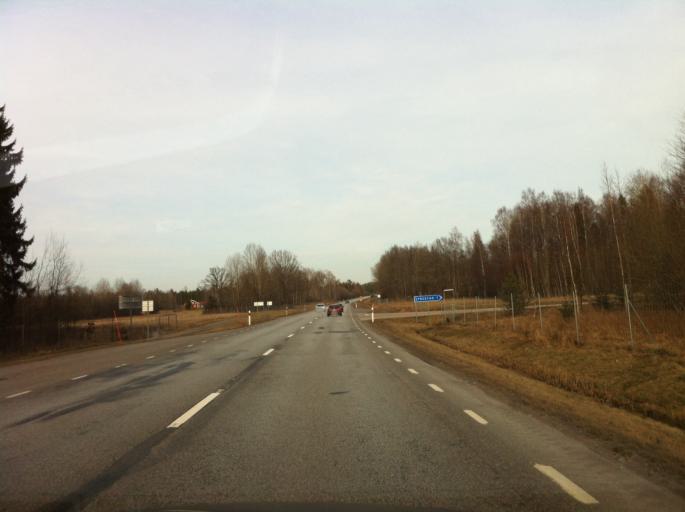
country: SE
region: Vaestra Goetaland
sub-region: Gullspangs Kommun
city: Gullspang
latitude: 58.8494
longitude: 13.9928
